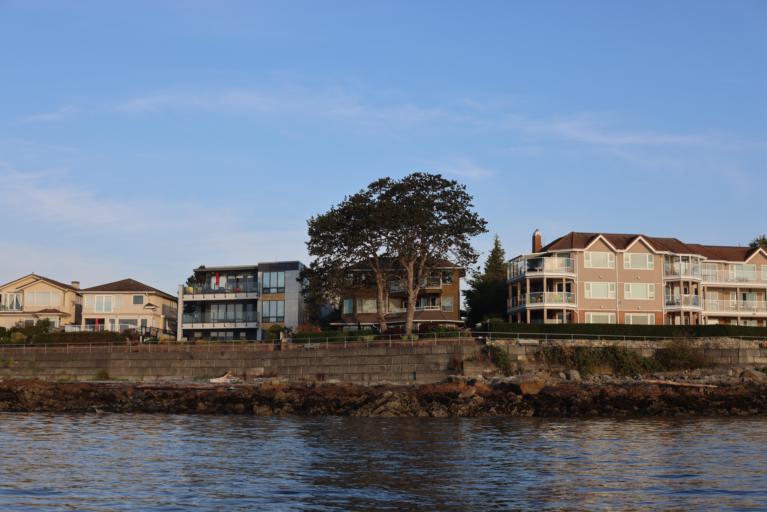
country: CA
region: British Columbia
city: North Saanich
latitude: 48.6458
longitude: -123.3926
